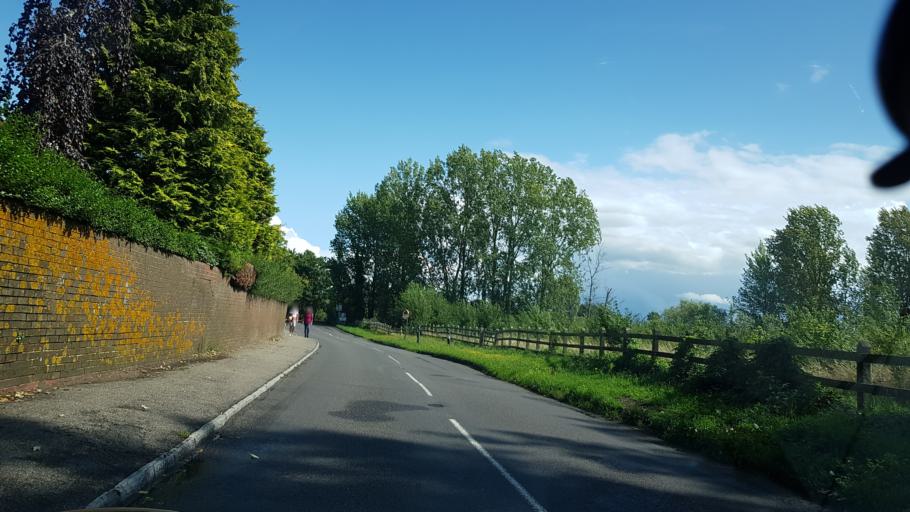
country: GB
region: England
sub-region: Surrey
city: Ripley
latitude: 51.3005
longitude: -0.5029
